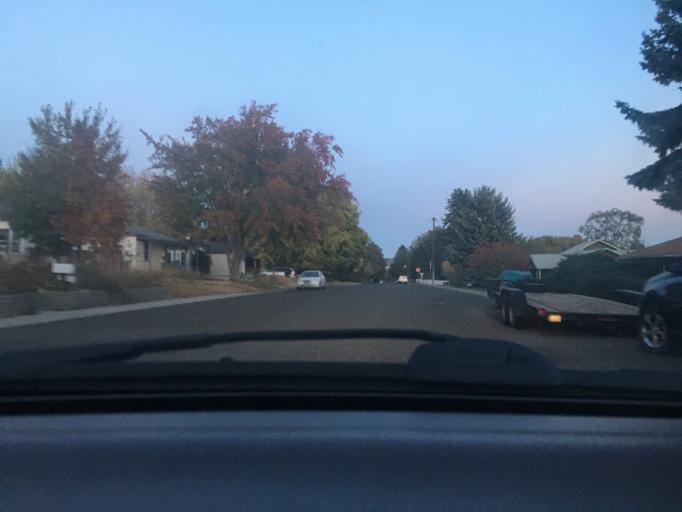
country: US
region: Washington
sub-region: Kittitas County
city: Ellensburg
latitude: 46.9927
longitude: -120.5348
